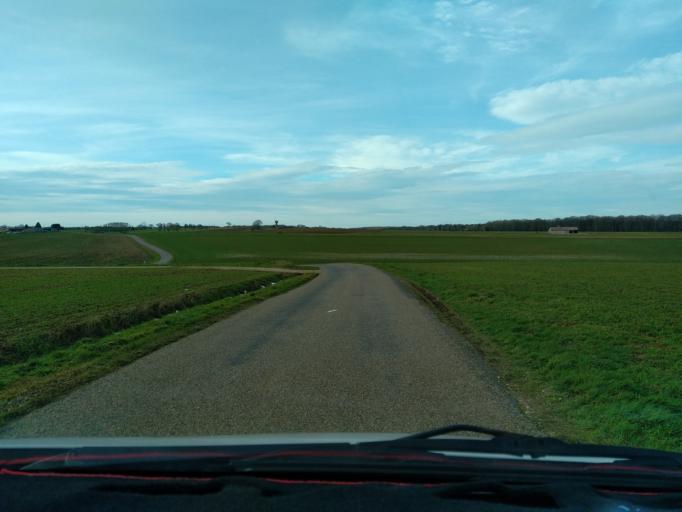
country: FR
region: Franche-Comte
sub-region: Departement de la Haute-Saone
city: Marnay
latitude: 47.3622
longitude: 5.6957
